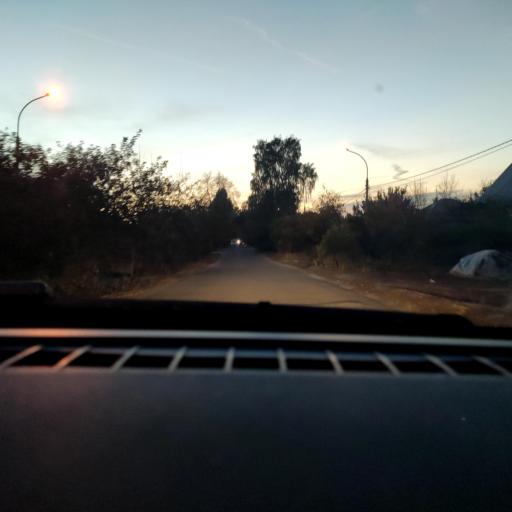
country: RU
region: Voronezj
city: Maslovka
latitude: 51.6157
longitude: 39.2667
